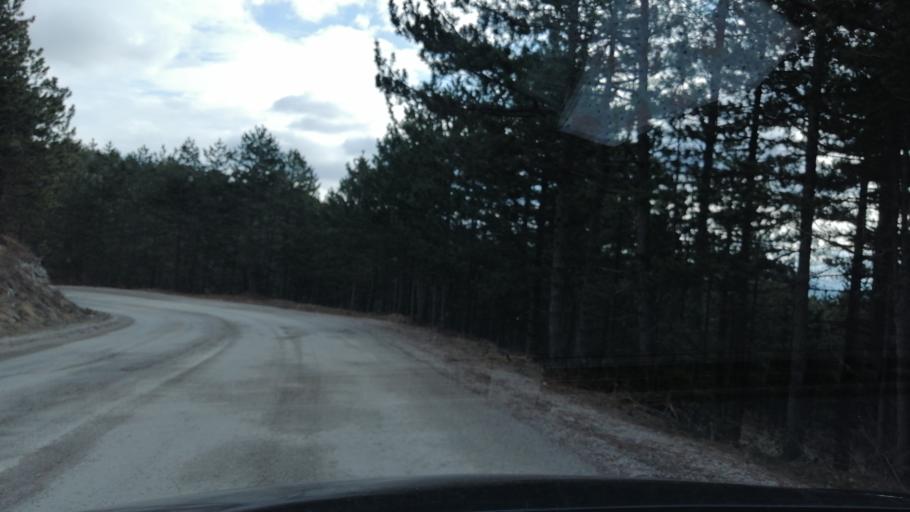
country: RS
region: Central Serbia
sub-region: Zlatiborski Okrug
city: Bajina Basta
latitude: 43.8776
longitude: 19.5638
